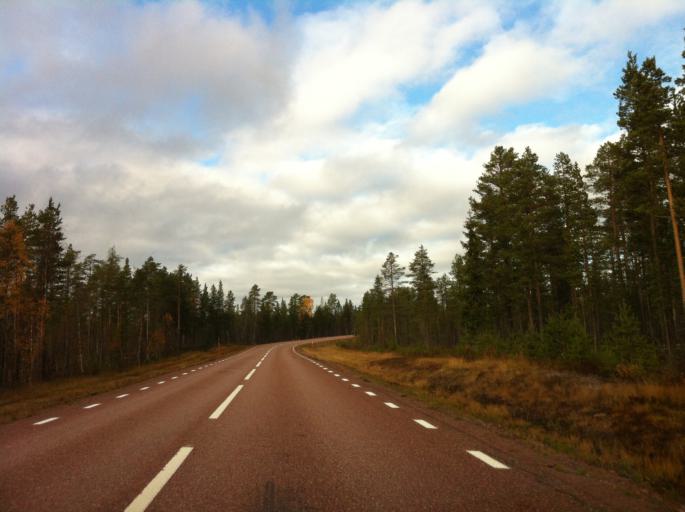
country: SE
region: Dalarna
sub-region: Alvdalens Kommun
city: AElvdalen
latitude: 61.5352
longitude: 13.3479
